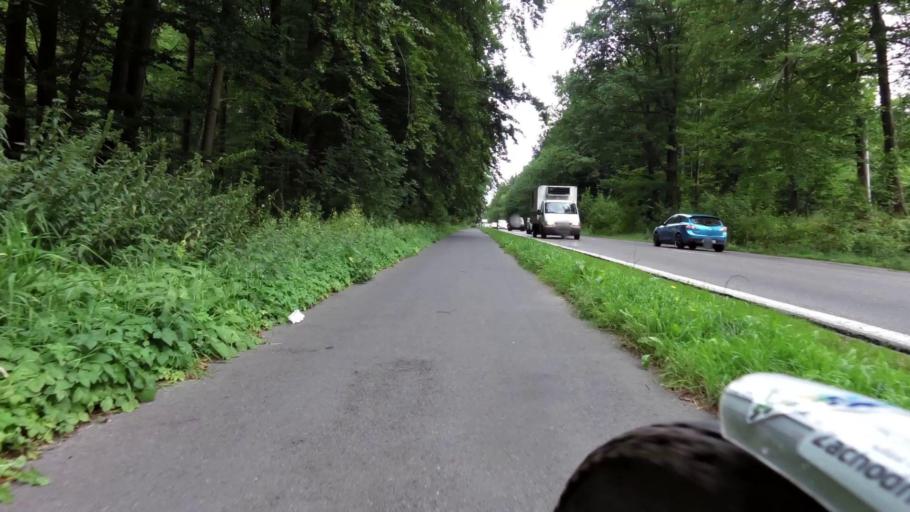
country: PL
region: West Pomeranian Voivodeship
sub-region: Koszalin
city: Koszalin
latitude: 54.2165
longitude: 16.1181
